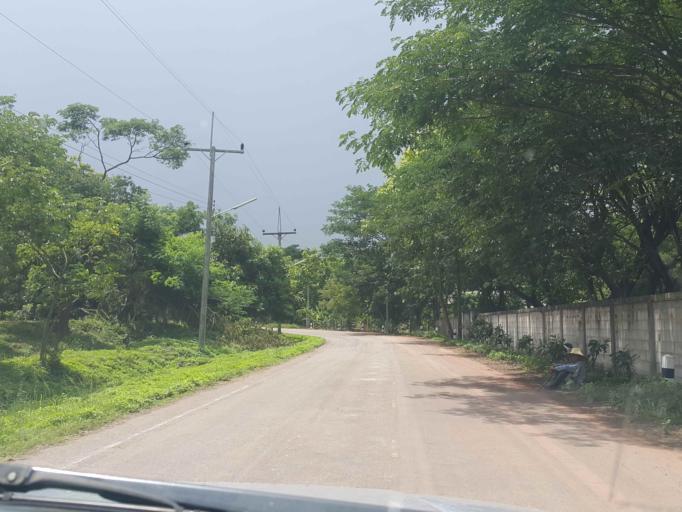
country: TH
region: Phayao
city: Dok Kham Tai
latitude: 19.0521
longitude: 99.9471
